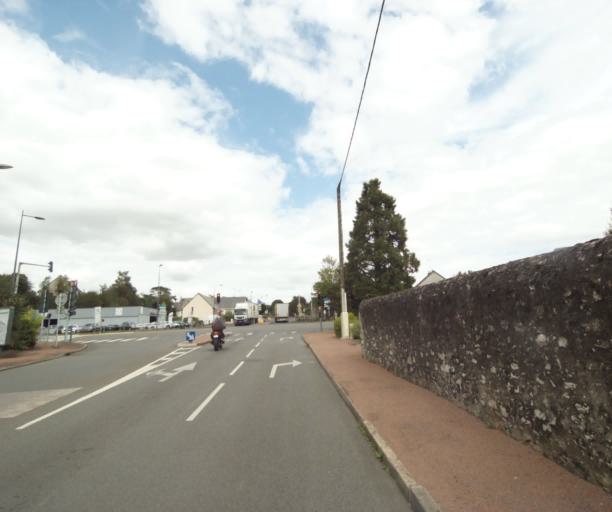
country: FR
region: Pays de la Loire
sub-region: Departement de la Sarthe
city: Sable-sur-Sarthe
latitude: 47.8436
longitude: -0.3331
